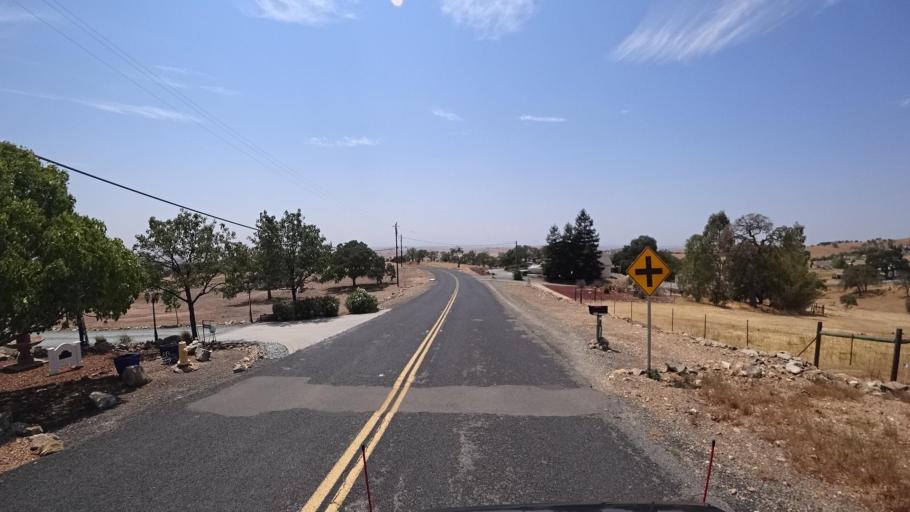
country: US
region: California
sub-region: Tuolumne County
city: Jamestown
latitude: 37.6530
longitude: -120.3506
